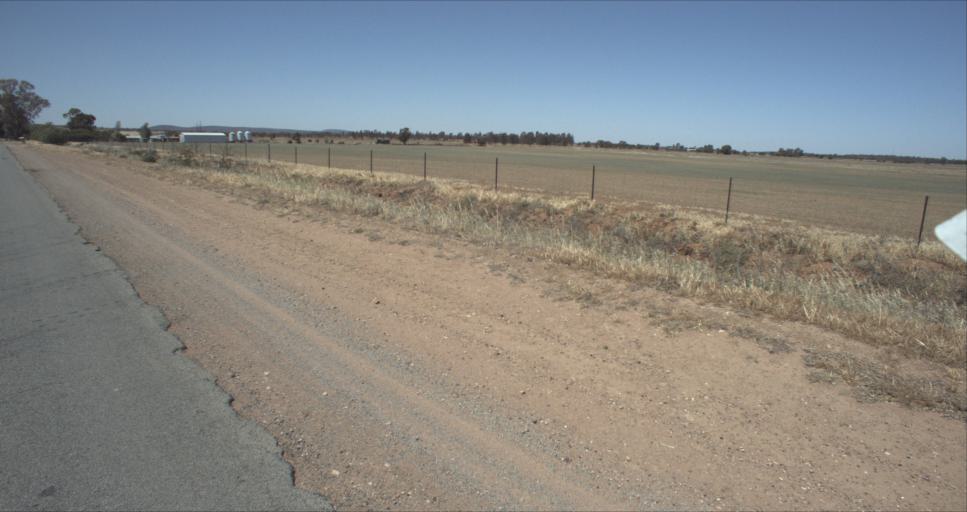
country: AU
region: New South Wales
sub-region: Leeton
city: Leeton
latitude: -34.5403
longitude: 146.4393
